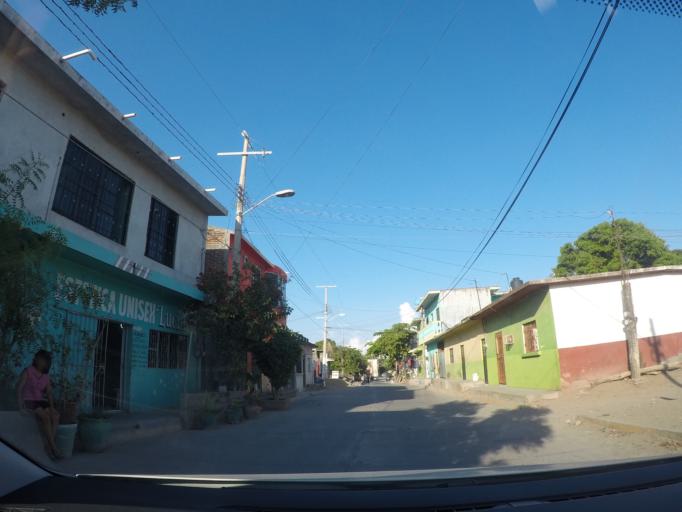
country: MX
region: Oaxaca
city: Juchitan de Zaragoza
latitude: 16.4393
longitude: -95.0299
